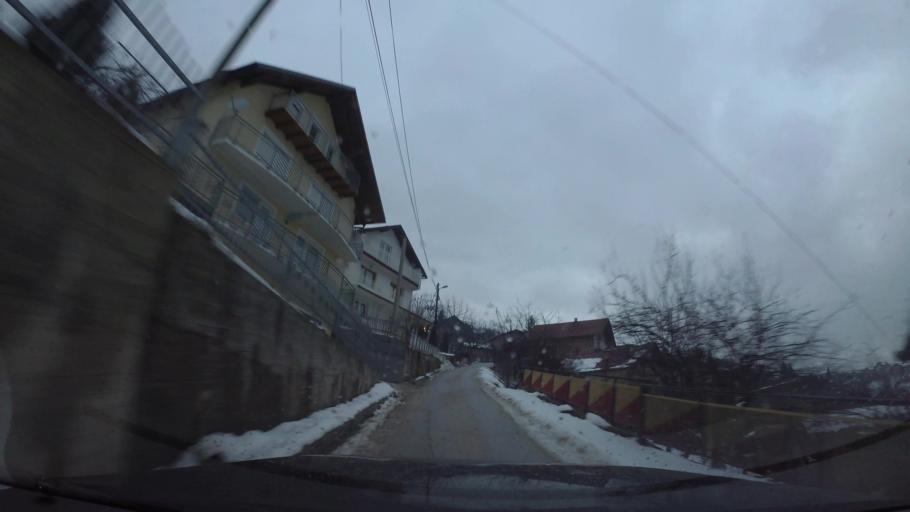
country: BA
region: Federation of Bosnia and Herzegovina
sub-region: Kanton Sarajevo
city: Sarajevo
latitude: 43.8551
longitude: 18.3381
